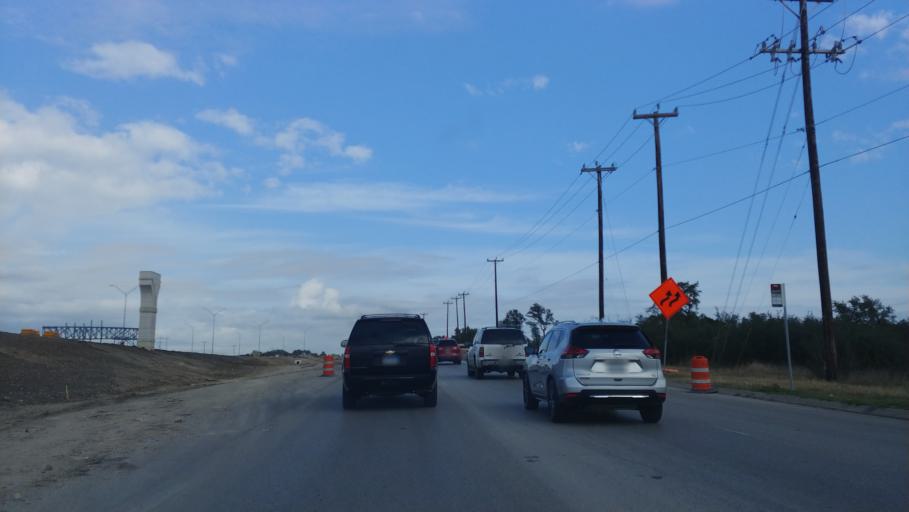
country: US
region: Texas
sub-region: Bexar County
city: Leon Valley
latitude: 29.4488
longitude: -98.7109
